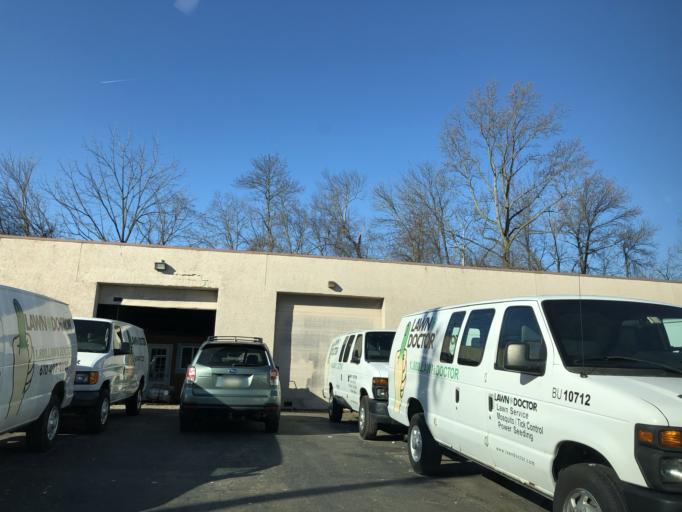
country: US
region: Pennsylvania
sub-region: Delaware County
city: Village Green-Green Ridge
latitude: 39.8474
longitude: -75.4336
